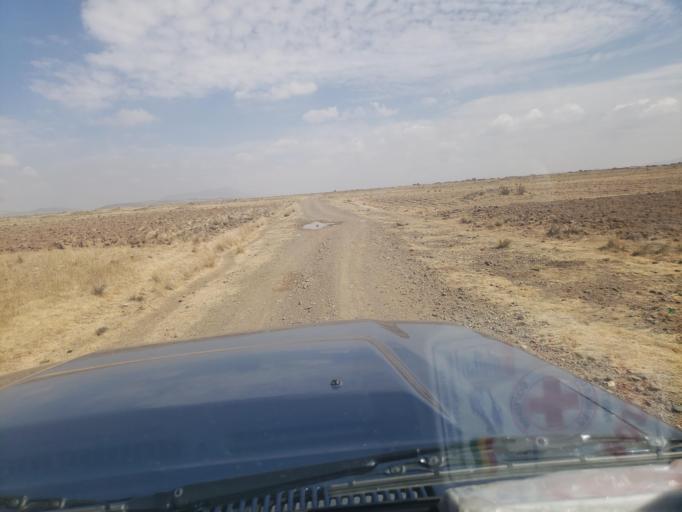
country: BO
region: La Paz
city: Batallas
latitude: -16.4227
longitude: -68.4076
